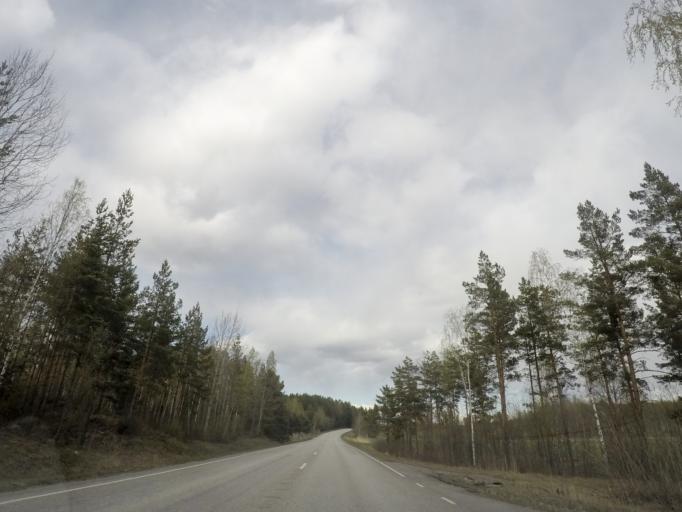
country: SE
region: Vaestmanland
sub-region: Kungsors Kommun
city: Kungsoer
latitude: 59.2924
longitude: 16.1944
